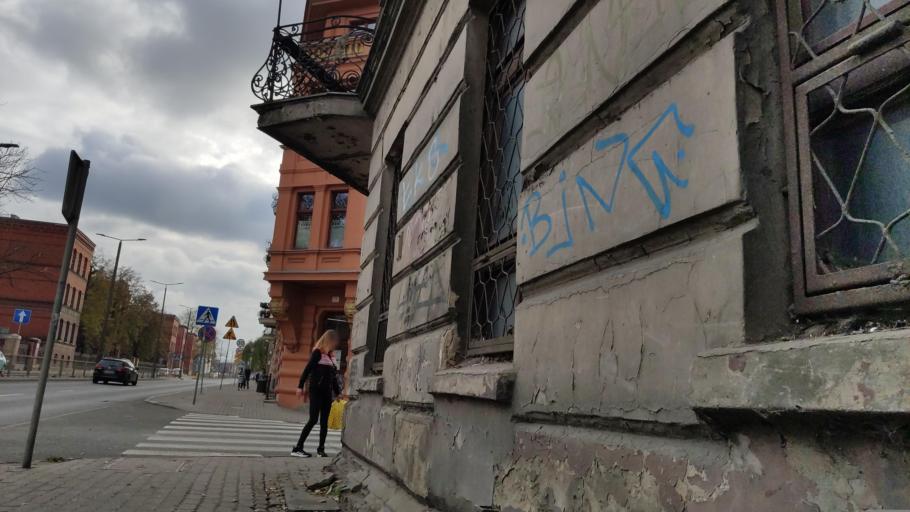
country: PL
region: Kujawsko-Pomorskie
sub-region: Powiat inowroclawski
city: Inowroclaw
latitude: 52.8046
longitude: 18.2484
